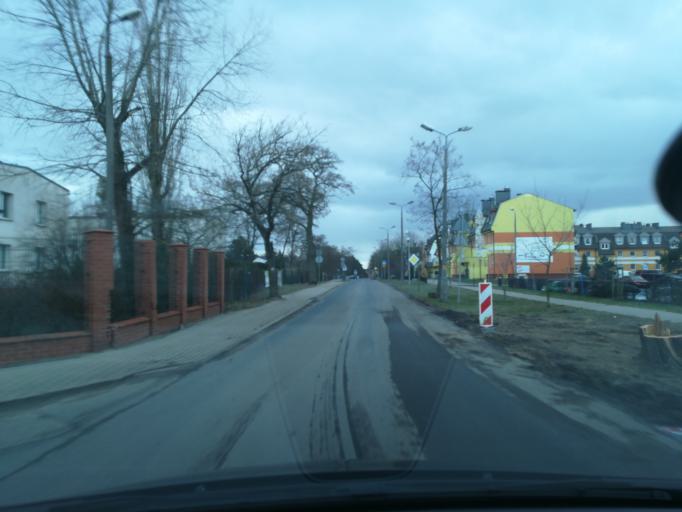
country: PL
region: Kujawsko-Pomorskie
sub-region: Powiat torunski
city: Lubicz Dolny
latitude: 52.9830
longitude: 18.6854
